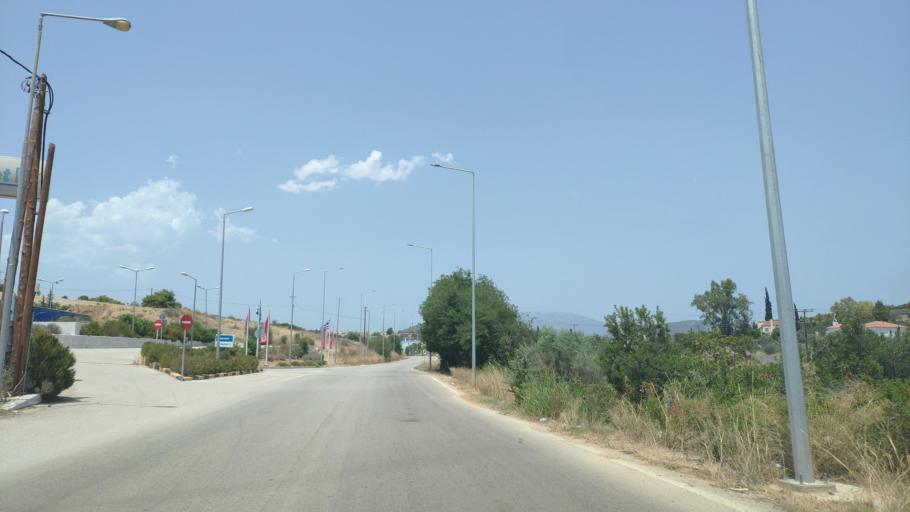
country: GR
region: Peloponnese
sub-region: Nomos Argolidos
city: Kranidi
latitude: 37.3609
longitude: 23.1626
